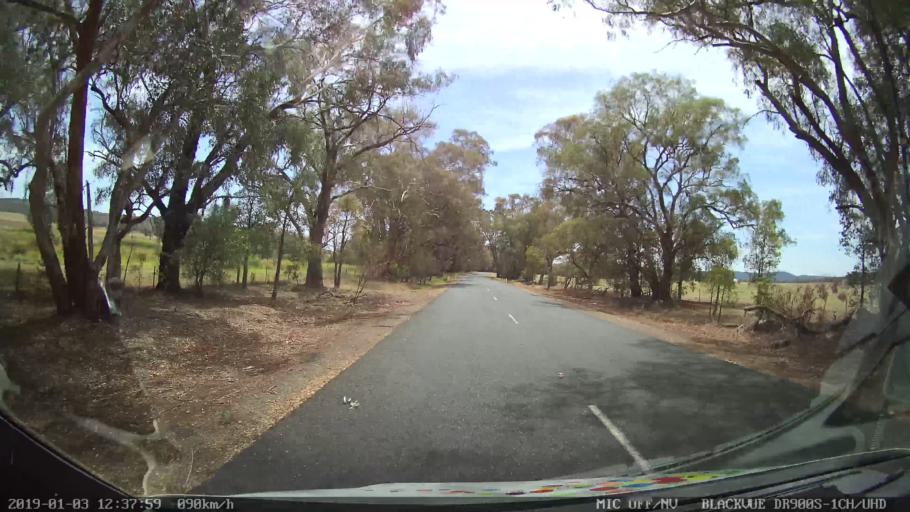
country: AU
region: New South Wales
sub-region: Weddin
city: Grenfell
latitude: -33.8377
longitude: 148.1905
